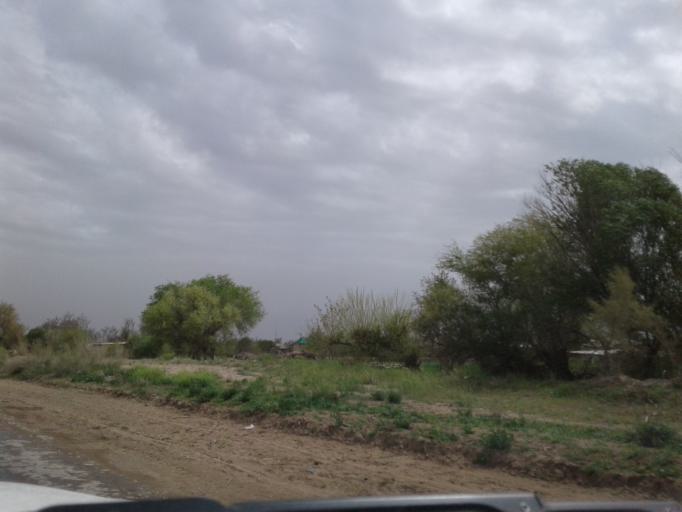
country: TM
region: Lebap
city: Atamyrat
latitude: 38.1704
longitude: 64.9116
